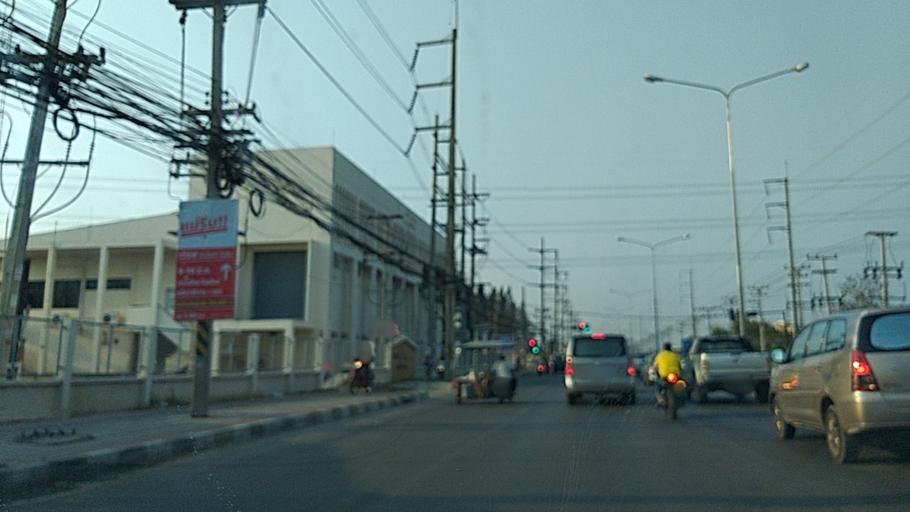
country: TH
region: Phra Nakhon Si Ayutthaya
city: Ban Bang Kadi Pathum Thani
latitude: 13.9744
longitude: 100.5506
